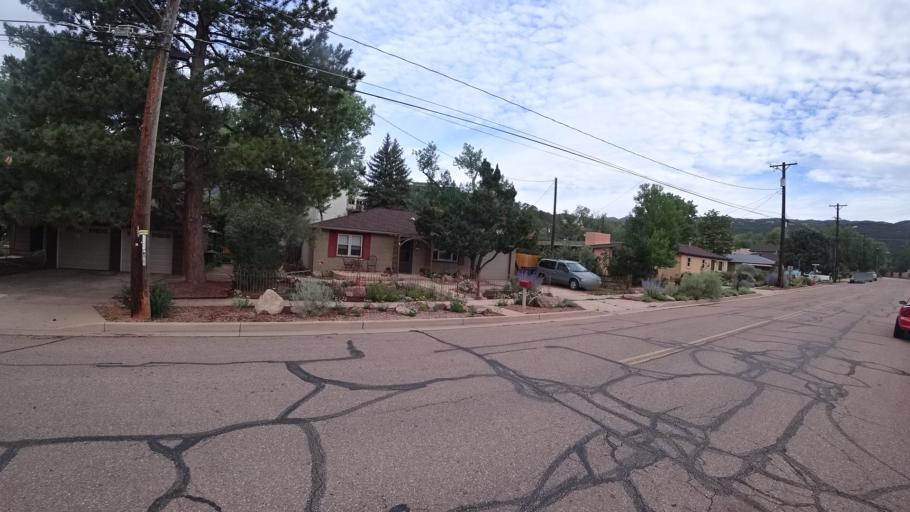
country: US
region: Colorado
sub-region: El Paso County
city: Manitou Springs
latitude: 38.8612
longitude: -104.8919
